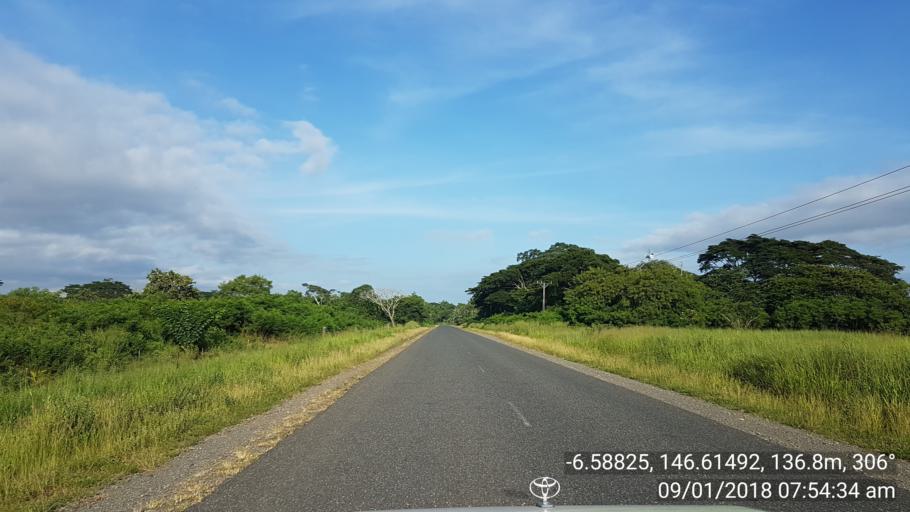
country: PG
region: Morobe
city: Lae
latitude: -6.5883
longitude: 146.6151
